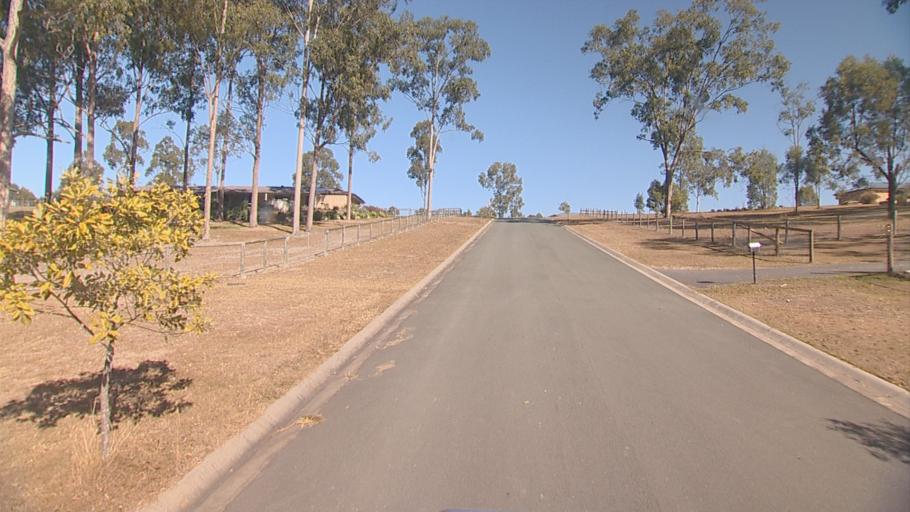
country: AU
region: Queensland
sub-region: Logan
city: Cedar Vale
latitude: -27.8707
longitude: 153.0383
